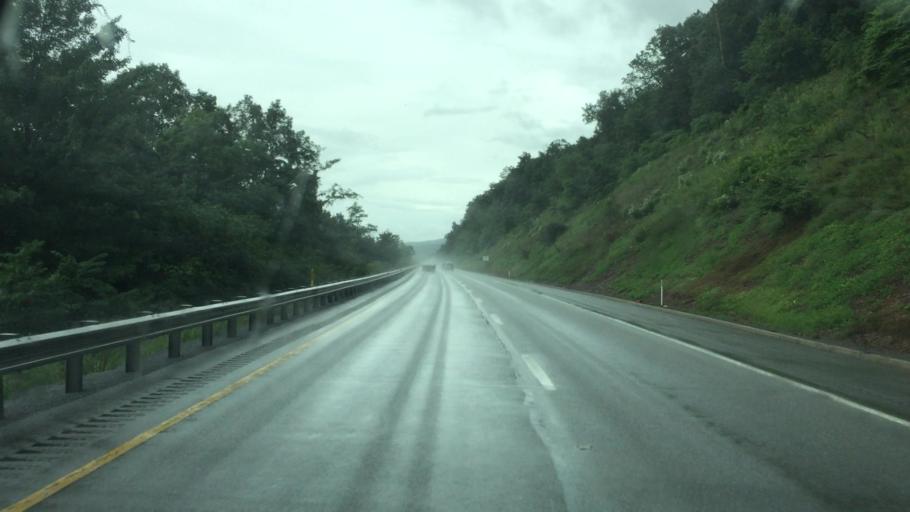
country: US
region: Pennsylvania
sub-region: Bedford County
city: Earlston
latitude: 39.8616
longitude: -78.2654
